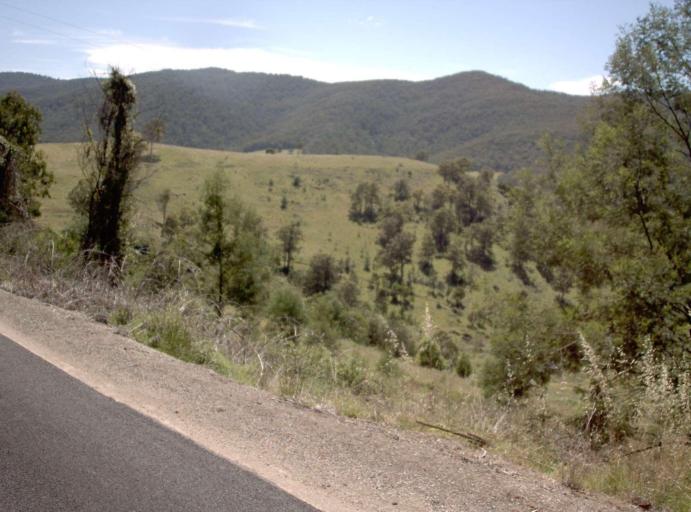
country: AU
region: Victoria
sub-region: East Gippsland
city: Lakes Entrance
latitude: -37.4253
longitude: 148.2018
